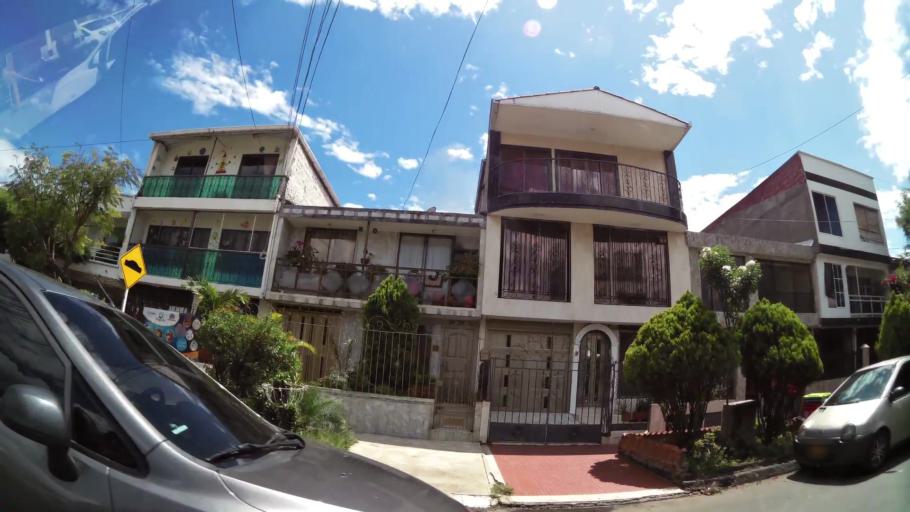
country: CO
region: Valle del Cauca
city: Cali
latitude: 3.3820
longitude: -76.5219
